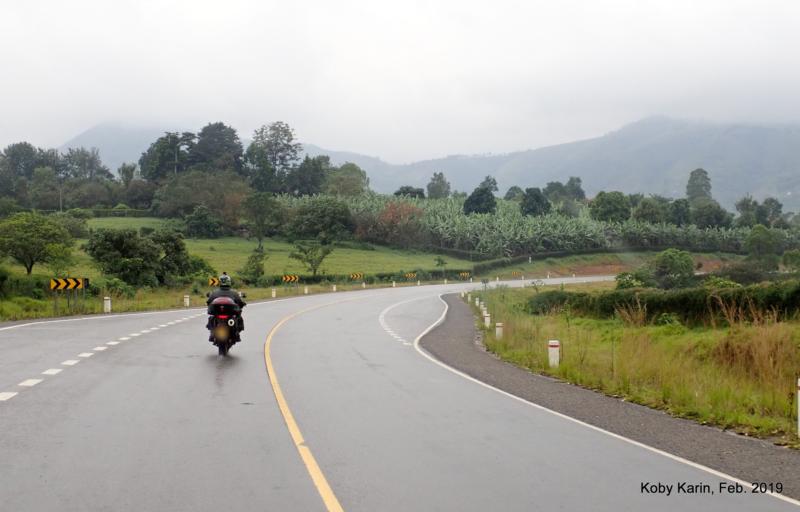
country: UG
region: Western Region
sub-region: Mitoma District
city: Mitoma
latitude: -0.6910
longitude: 30.1680
